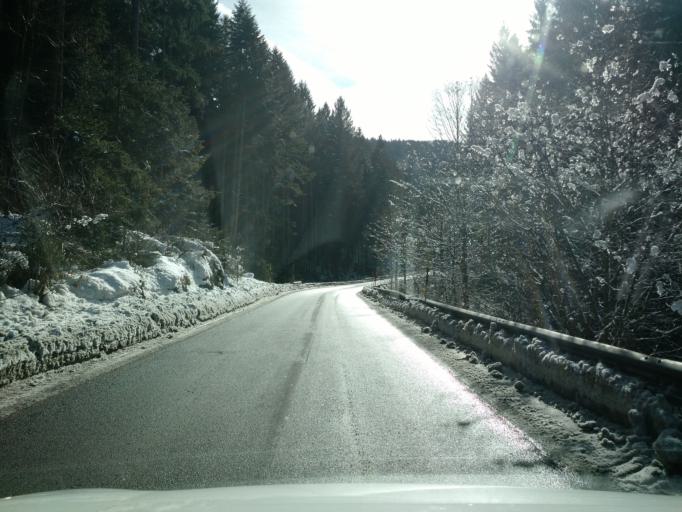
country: IT
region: Veneto
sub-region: Provincia di Vicenza
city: Canove di Roana
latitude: 45.8451
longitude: 11.4654
